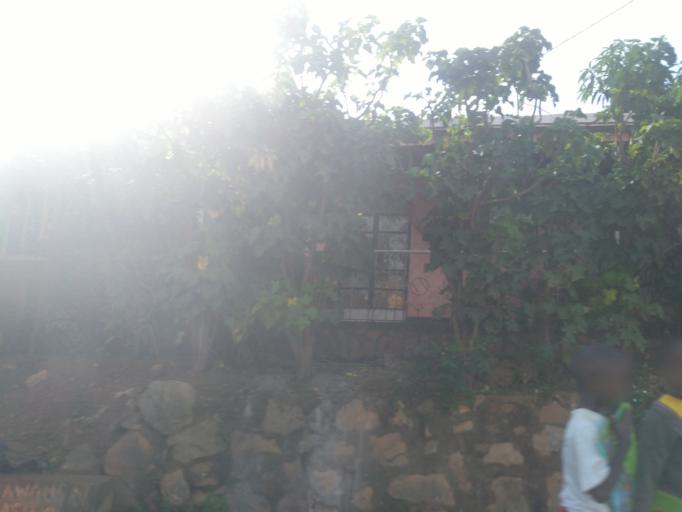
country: UG
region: Central Region
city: Kampala Central Division
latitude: 0.3581
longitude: 32.5698
